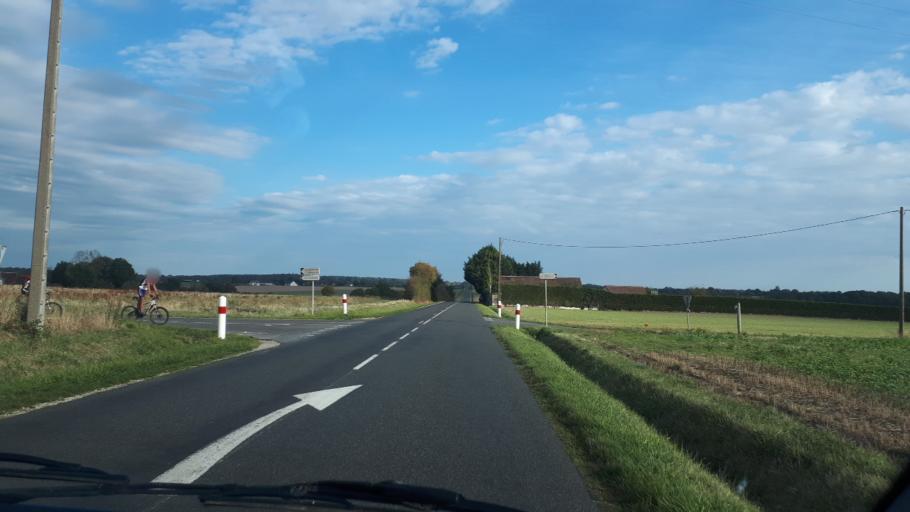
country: FR
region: Centre
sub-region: Departement du Loir-et-Cher
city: Sarge-sur-Braye
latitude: 47.9055
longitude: 0.9303
